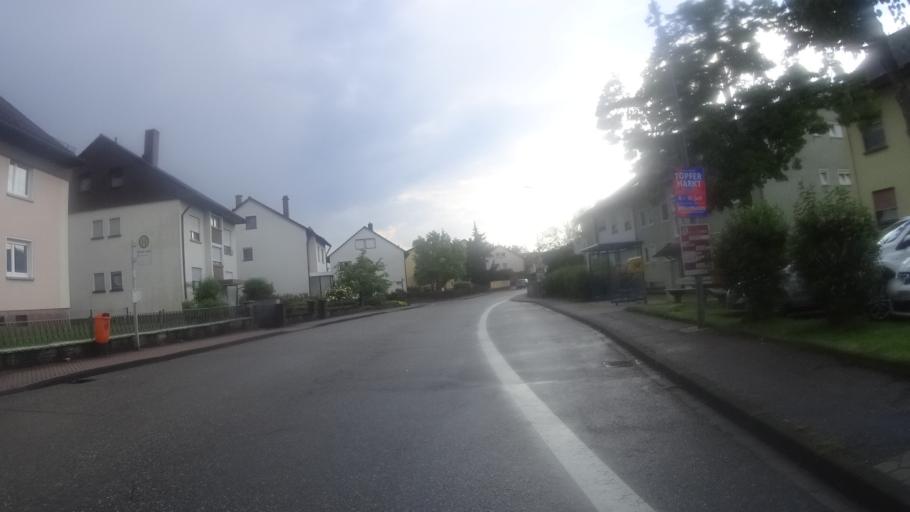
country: DE
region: Baden-Wuerttemberg
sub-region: Karlsruhe Region
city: Durmersheim
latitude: 48.9253
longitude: 8.2661
